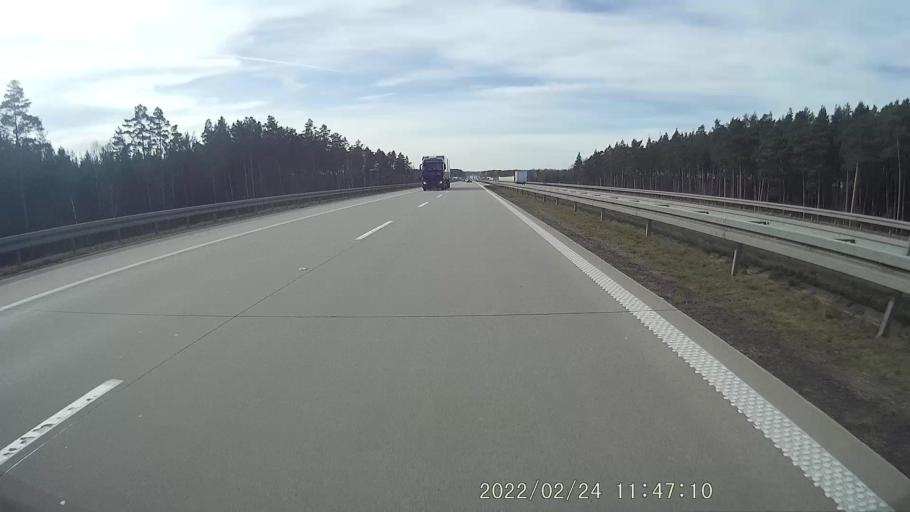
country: PL
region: Lower Silesian Voivodeship
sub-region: Powiat polkowicki
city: Radwanice
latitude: 51.5742
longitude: 15.9490
